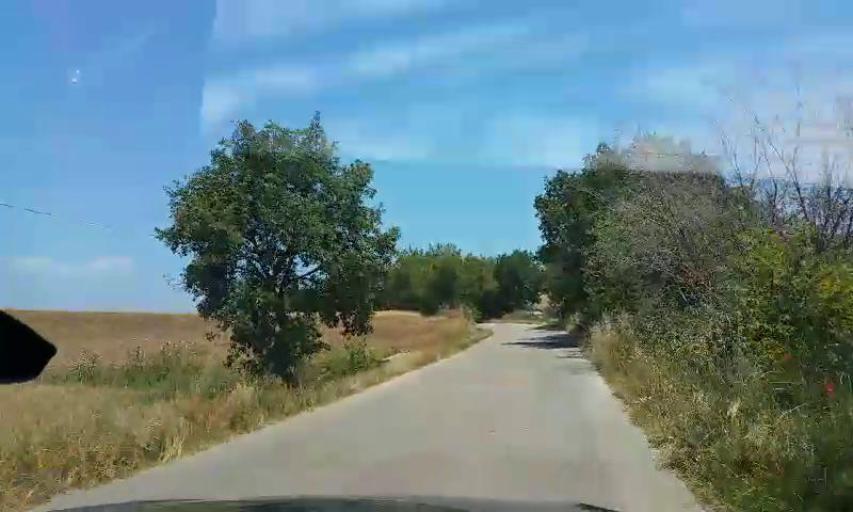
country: IT
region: Molise
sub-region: Provincia di Campobasso
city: Guglionesi
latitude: 41.9533
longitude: 14.9009
